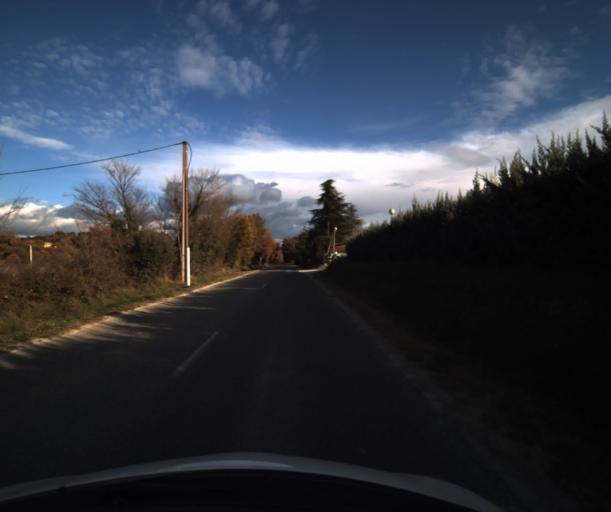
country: FR
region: Provence-Alpes-Cote d'Azur
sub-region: Departement du Vaucluse
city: Pertuis
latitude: 43.6958
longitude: 5.5268
